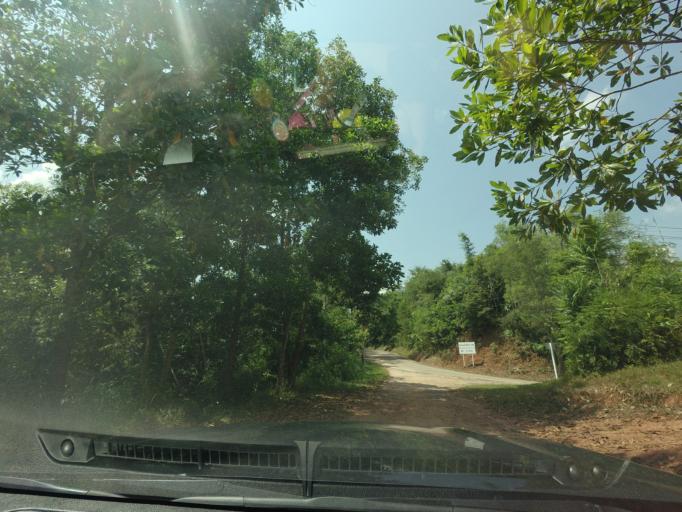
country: TH
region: Nan
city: Bo Kluea
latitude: 19.0151
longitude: 101.2054
